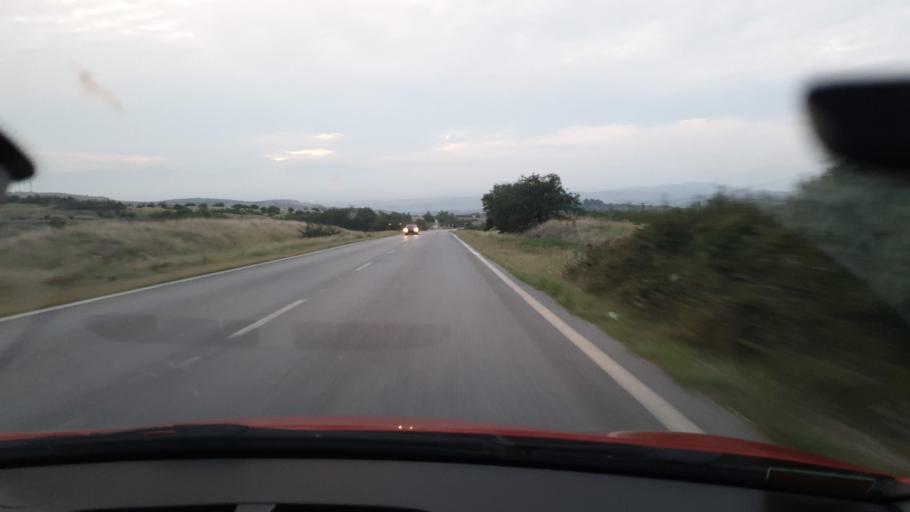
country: GR
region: Central Macedonia
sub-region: Nomos Kilkis
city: Polykastro
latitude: 41.0089
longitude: 22.6834
